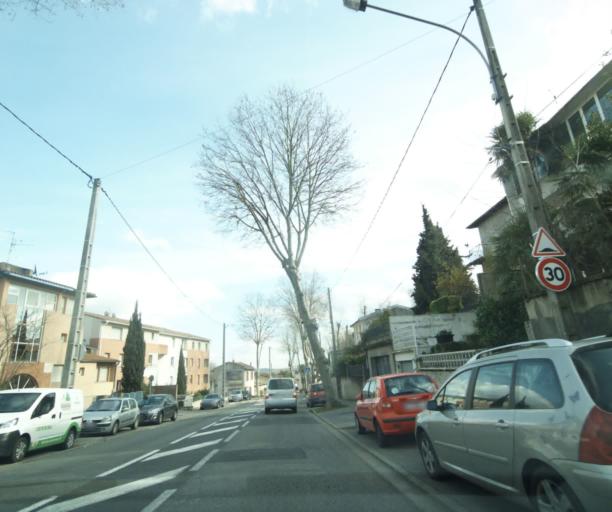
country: FR
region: Midi-Pyrenees
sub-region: Departement de la Haute-Garonne
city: Balma
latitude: 43.5987
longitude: 1.4802
